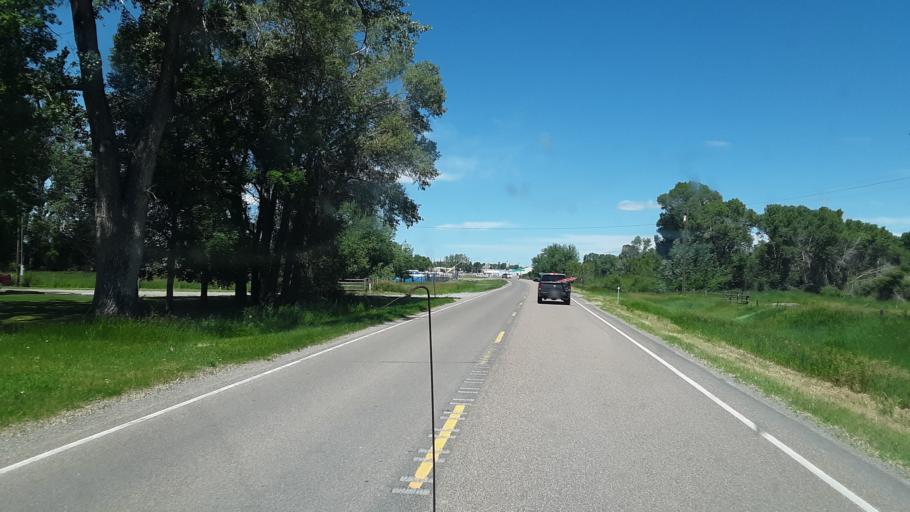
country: US
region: Montana
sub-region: Teton County
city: Choteau
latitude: 47.8012
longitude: -112.1732
